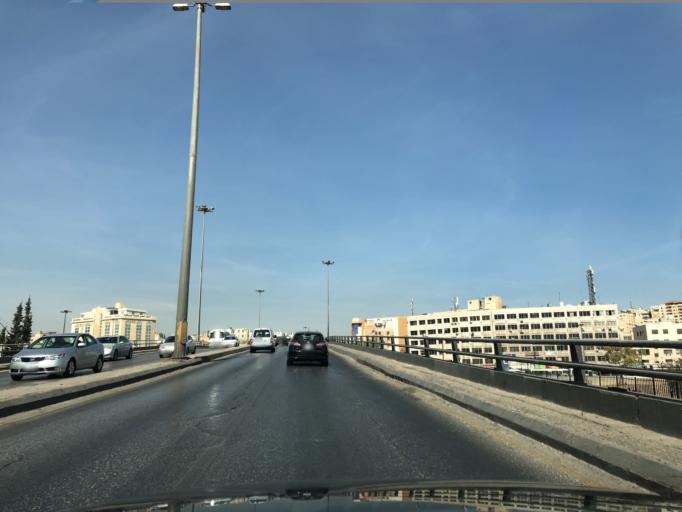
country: JO
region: Amman
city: Al Jubayhah
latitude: 31.9846
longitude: 35.8994
